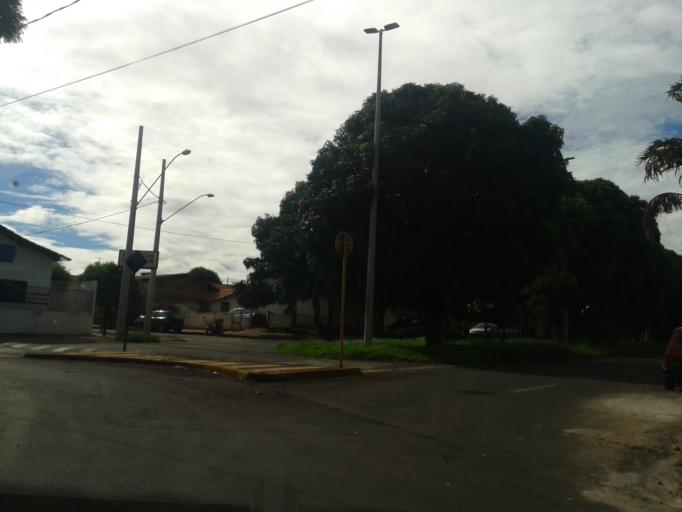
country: BR
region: Minas Gerais
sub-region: Ituiutaba
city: Ituiutaba
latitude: -18.9886
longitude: -49.4680
